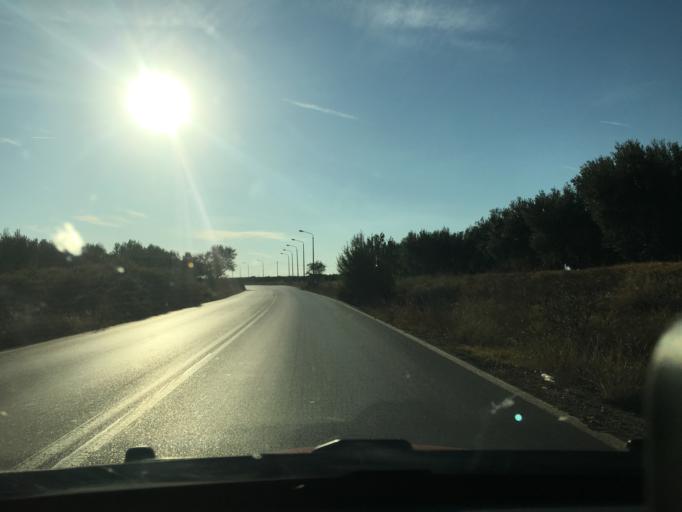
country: GR
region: Central Macedonia
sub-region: Nomos Chalkidikis
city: Olynthos
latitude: 40.2838
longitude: 23.3644
